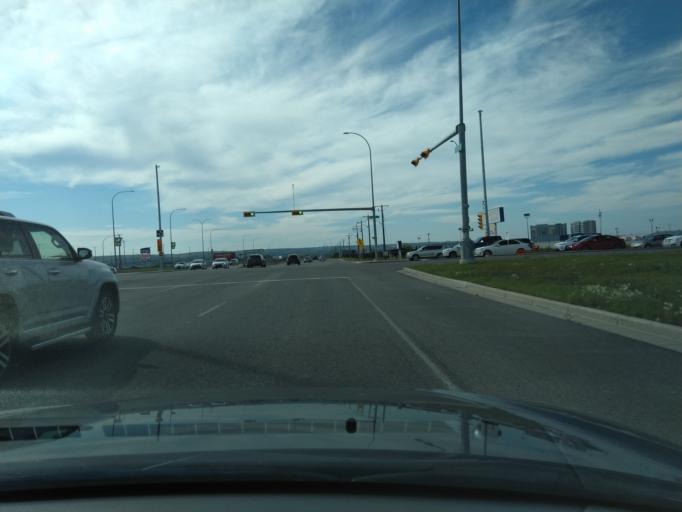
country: CA
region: Alberta
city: Calgary
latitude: 51.1398
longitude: -114.0011
